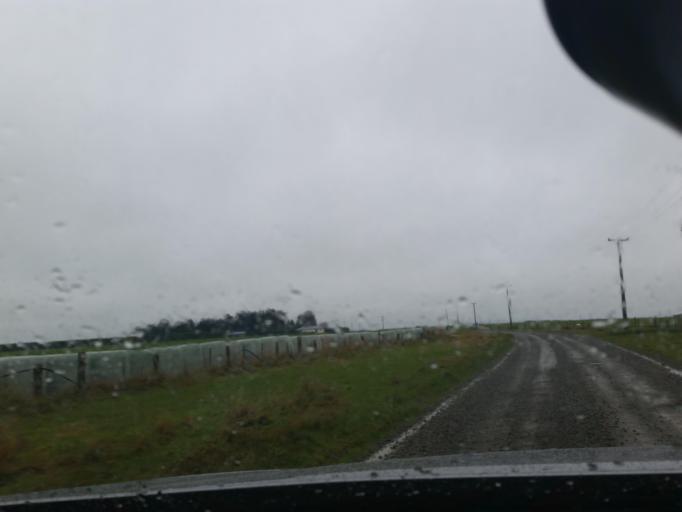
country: NZ
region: Southland
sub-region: Southland District
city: Winton
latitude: -46.1834
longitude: 168.2028
